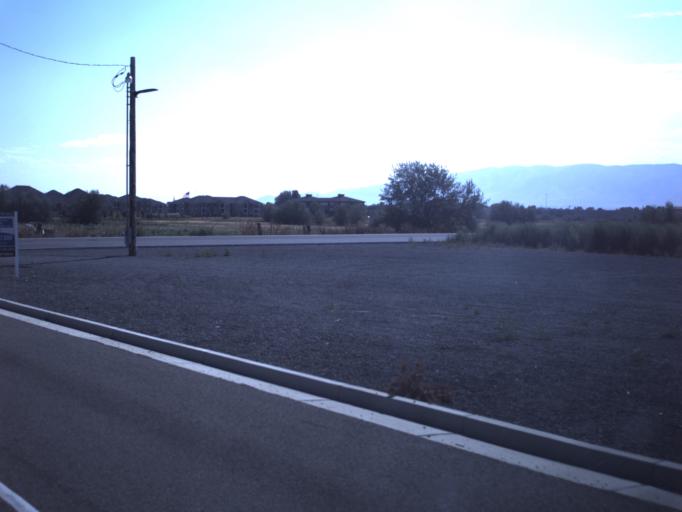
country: US
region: Utah
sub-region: Utah County
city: American Fork
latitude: 40.3644
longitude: -111.7692
